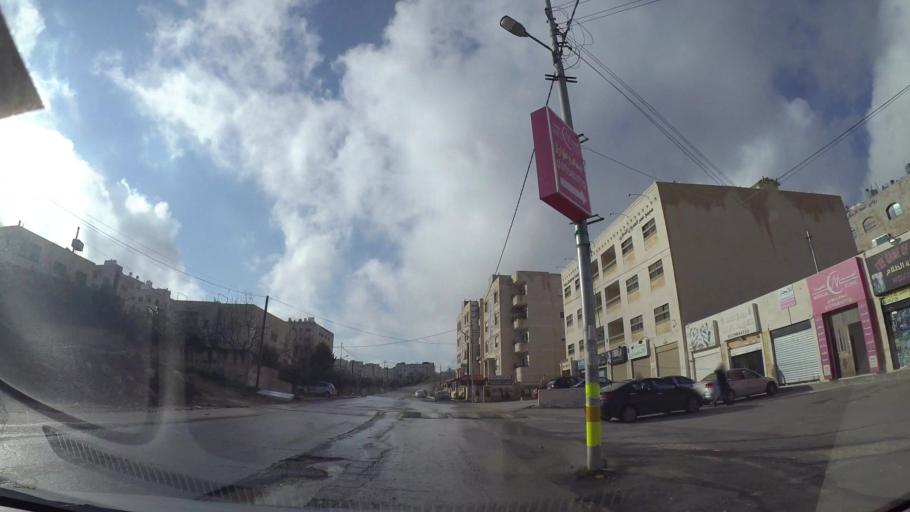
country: JO
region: Amman
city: Al Jubayhah
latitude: 32.0554
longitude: 35.8972
